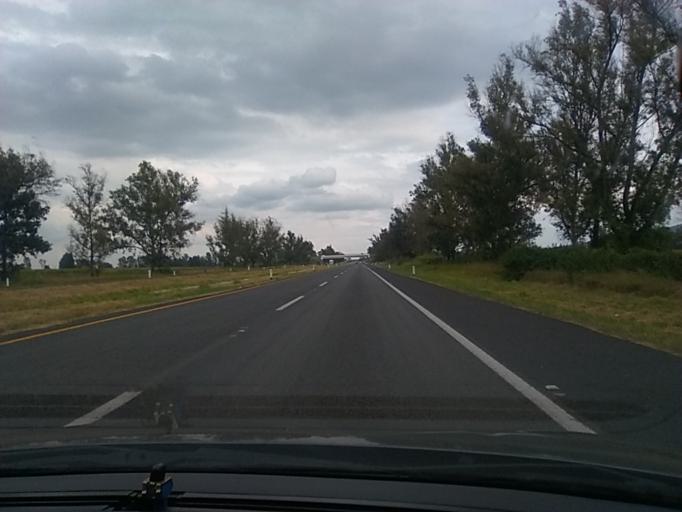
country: MX
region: Jalisco
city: Ocotlan
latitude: 20.3890
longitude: -102.7143
